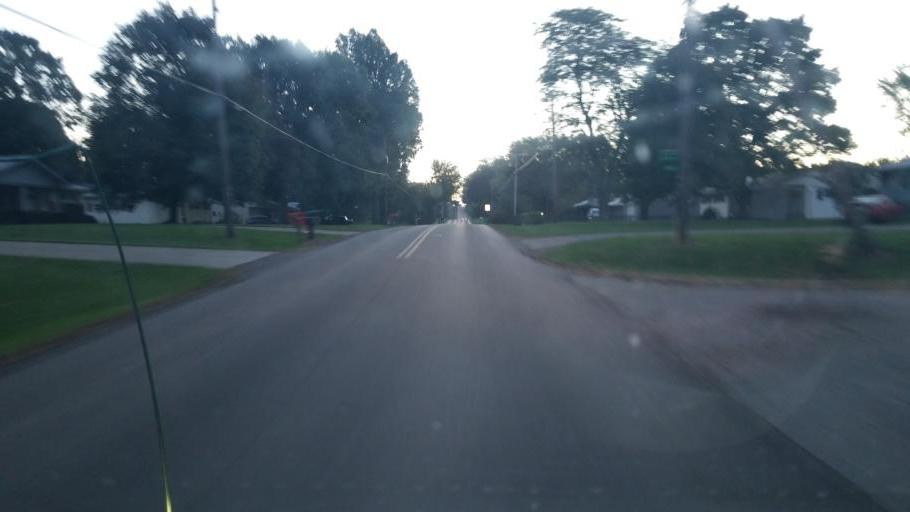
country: US
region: Ohio
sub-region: Wayne County
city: Apple Creek
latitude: 40.7409
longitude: -81.8124
